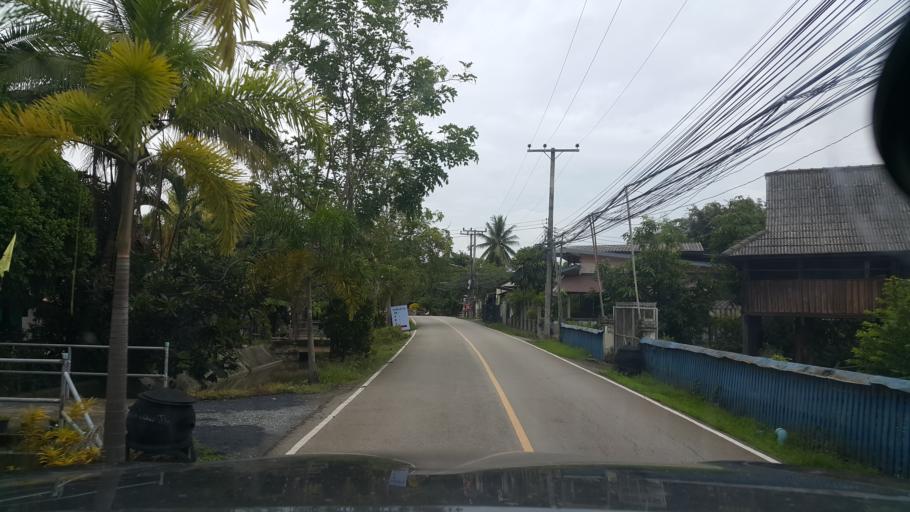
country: TH
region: Chiang Mai
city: Mae On
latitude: 18.8294
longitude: 99.1836
